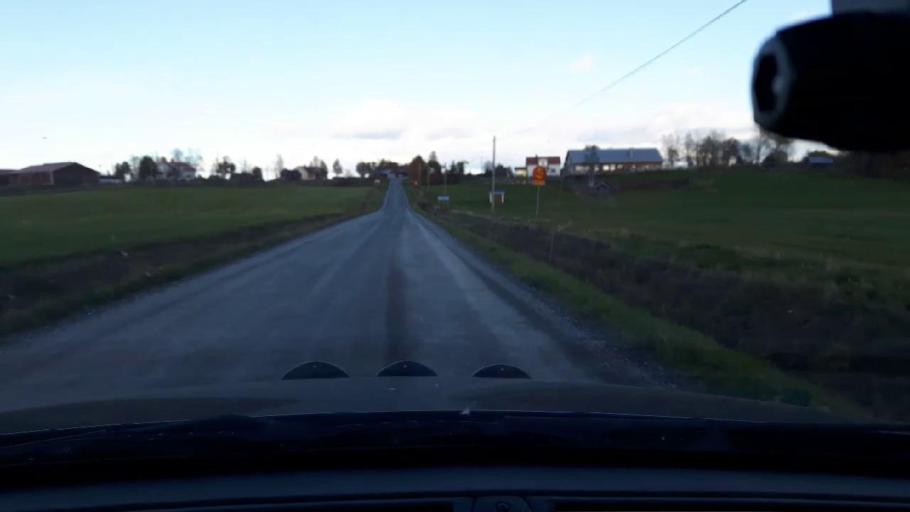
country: SE
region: Jaemtland
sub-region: Krokoms Kommun
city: Krokom
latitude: 63.0773
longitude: 14.2726
